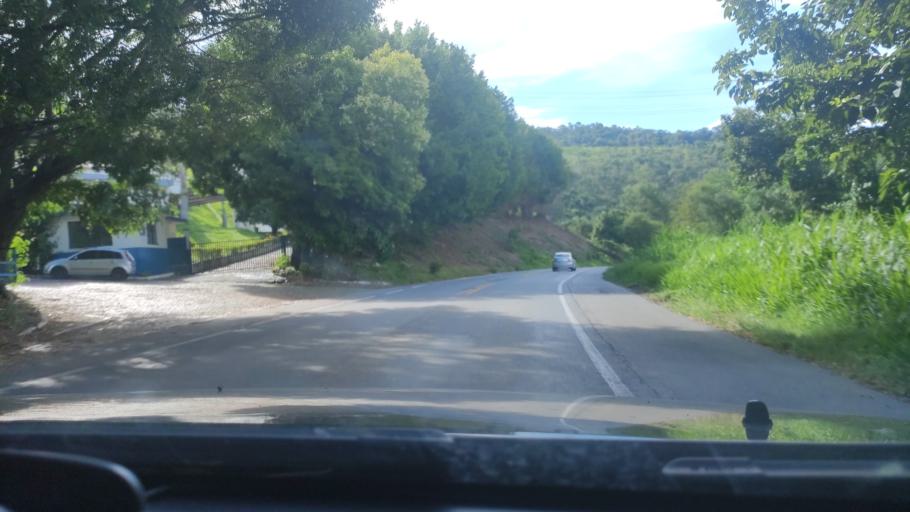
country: BR
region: Sao Paulo
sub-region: Aguas De Lindoia
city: Aguas de Lindoia
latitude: -22.5181
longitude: -46.6670
